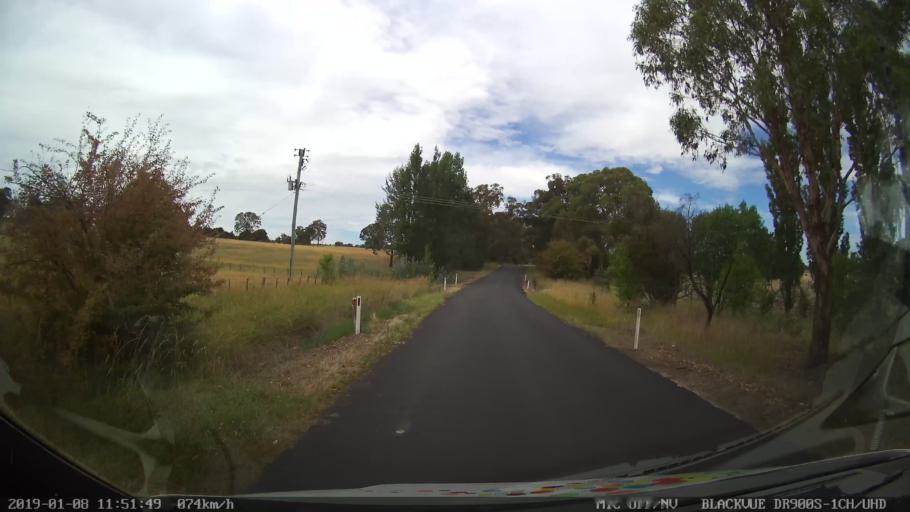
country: AU
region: New South Wales
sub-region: Armidale Dumaresq
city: Armidale
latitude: -30.3971
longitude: 151.5610
